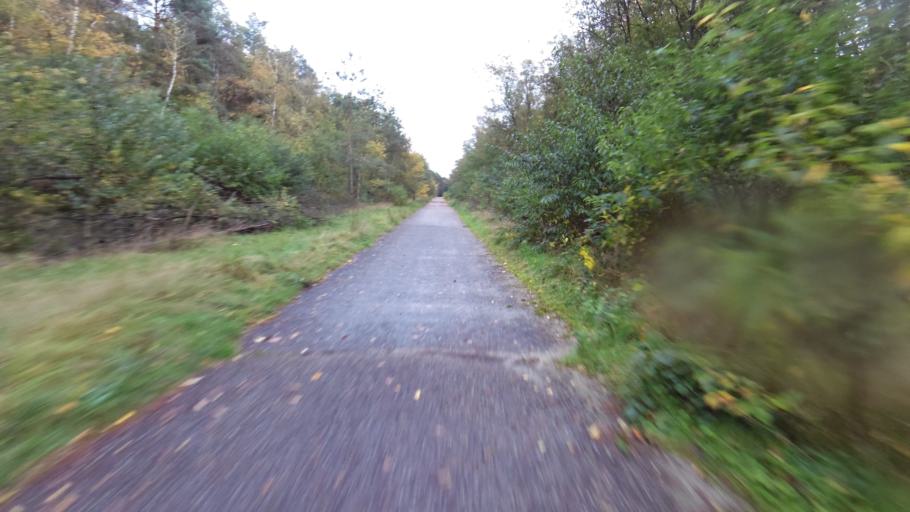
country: NL
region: Gelderland
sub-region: Gemeente Renkum
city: Wolfheze
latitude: 52.0032
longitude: 5.8079
